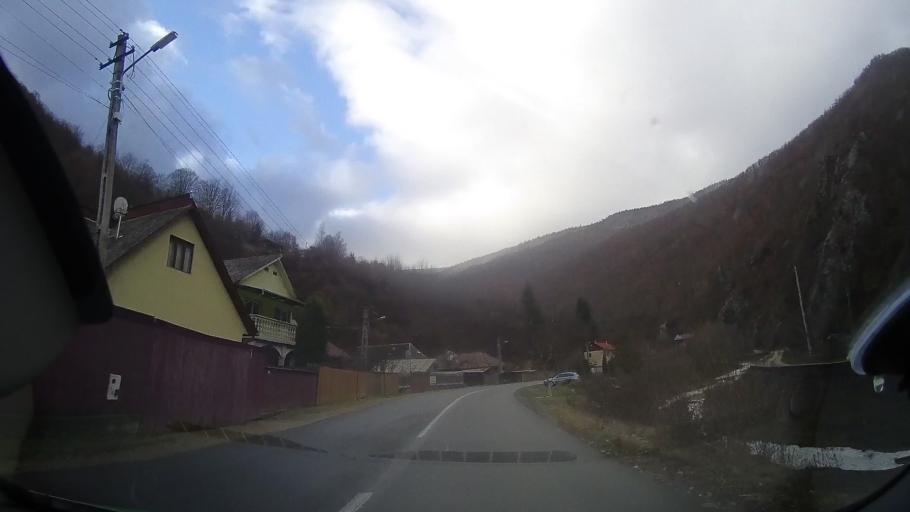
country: RO
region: Cluj
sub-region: Comuna Valea Ierii
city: Valea Ierii
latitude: 46.6851
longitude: 23.2795
